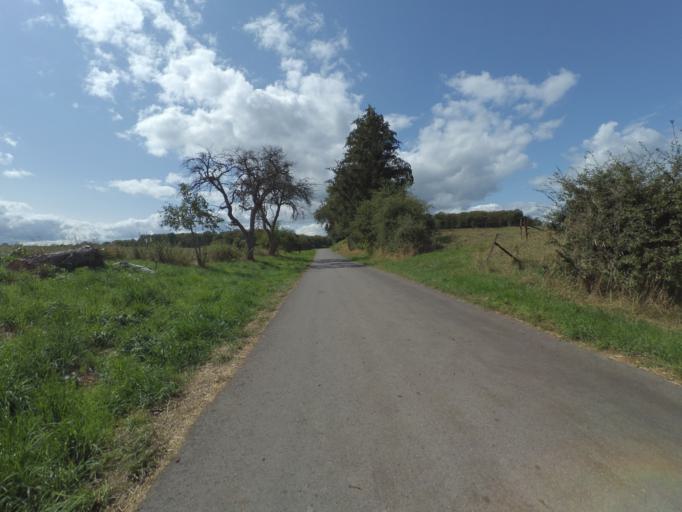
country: LU
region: Grevenmacher
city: Gonderange
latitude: 49.6850
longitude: 6.2819
